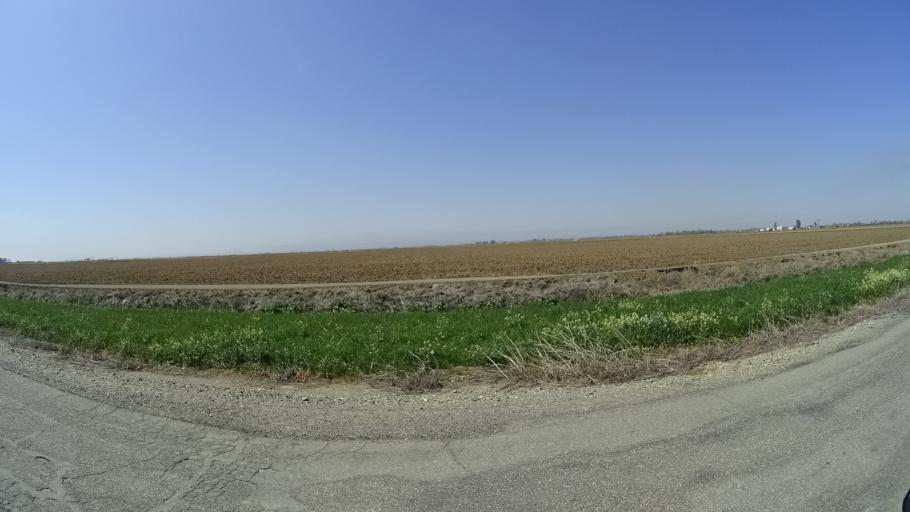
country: US
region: California
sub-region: Glenn County
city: Willows
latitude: 39.5075
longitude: -122.1368
